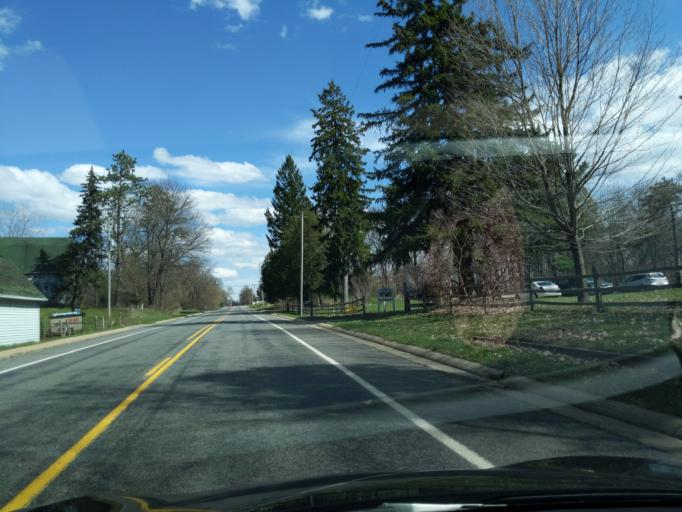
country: US
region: Michigan
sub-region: Ingham County
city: Mason
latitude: 42.5514
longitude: -84.3855
